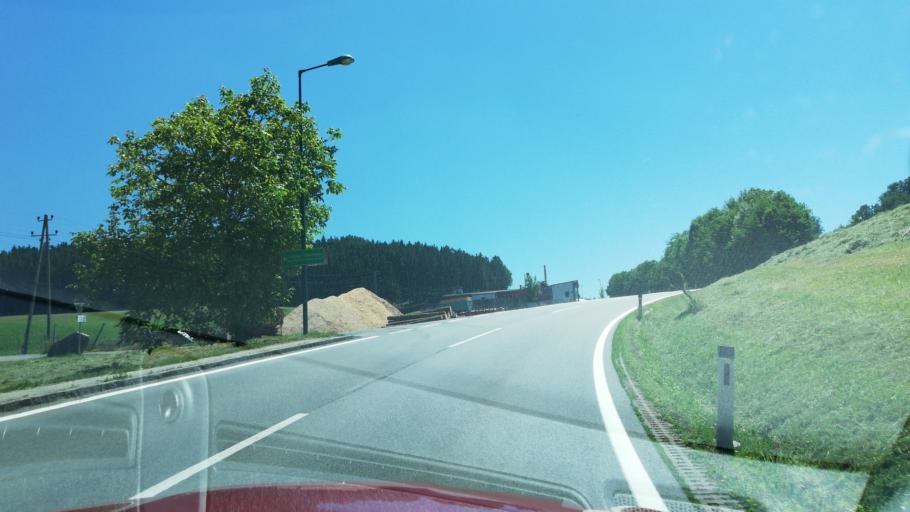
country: AT
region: Upper Austria
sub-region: Politischer Bezirk Vocklabruck
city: Niederthalheim
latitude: 48.1367
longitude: 13.7355
